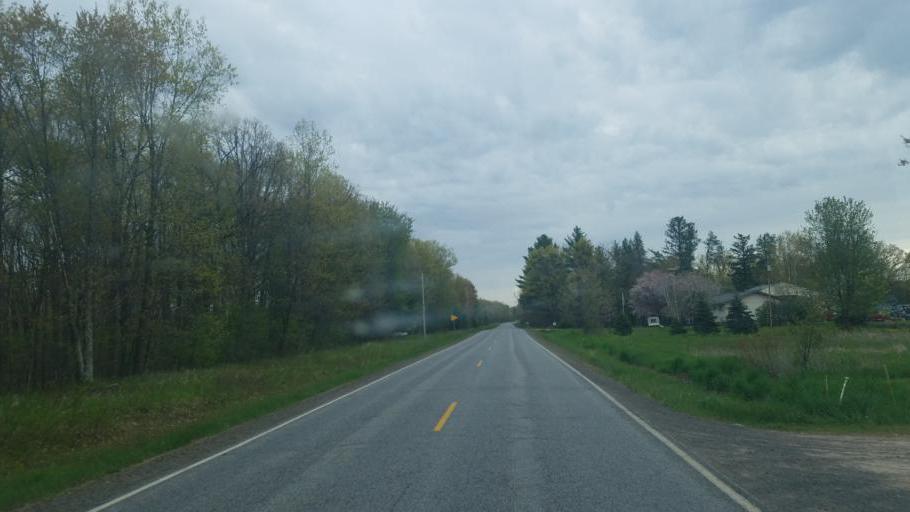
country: US
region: Wisconsin
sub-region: Wood County
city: Marshfield
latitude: 44.4040
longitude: -90.1603
